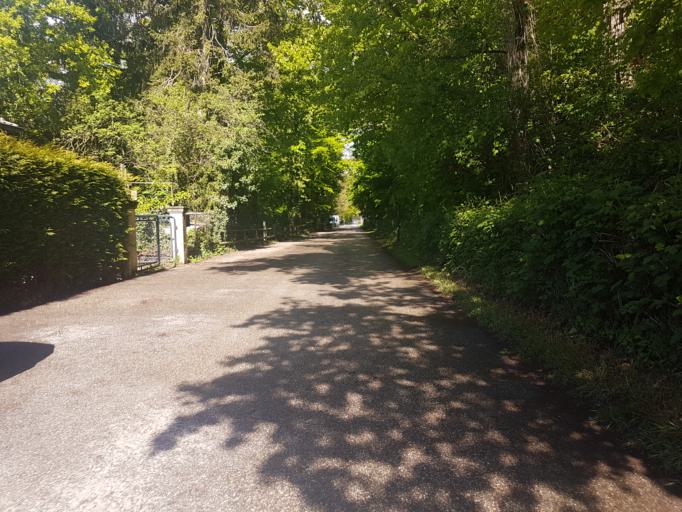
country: CH
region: Vaud
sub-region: Nyon District
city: Perroy
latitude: 46.4647
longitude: 6.3848
